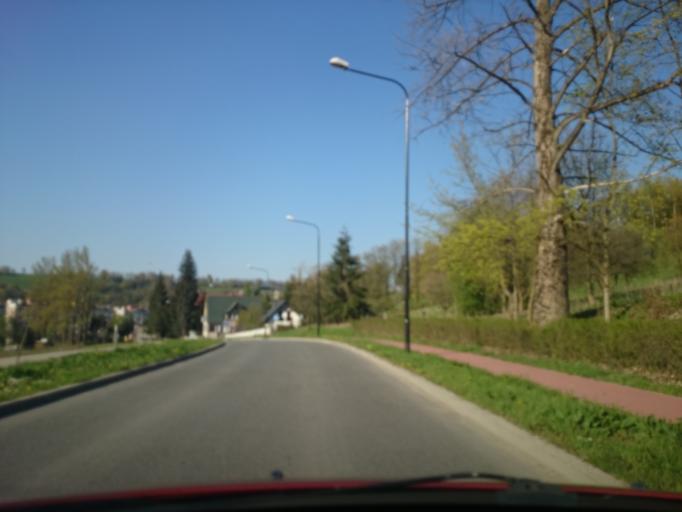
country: PL
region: Lower Silesian Voivodeship
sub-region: Powiat klodzki
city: Duszniki-Zdroj
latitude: 50.3984
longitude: 16.3915
